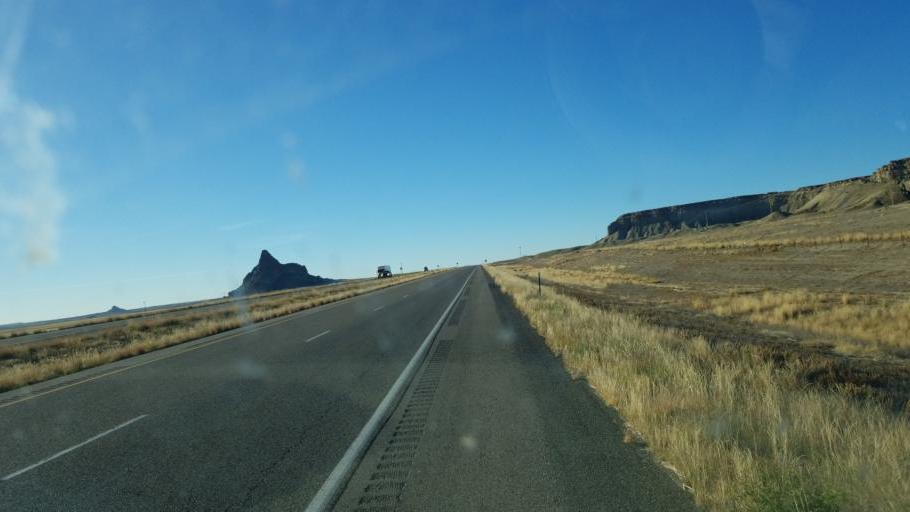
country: US
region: New Mexico
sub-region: San Juan County
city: Shiprock
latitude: 36.6059
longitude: -108.7045
